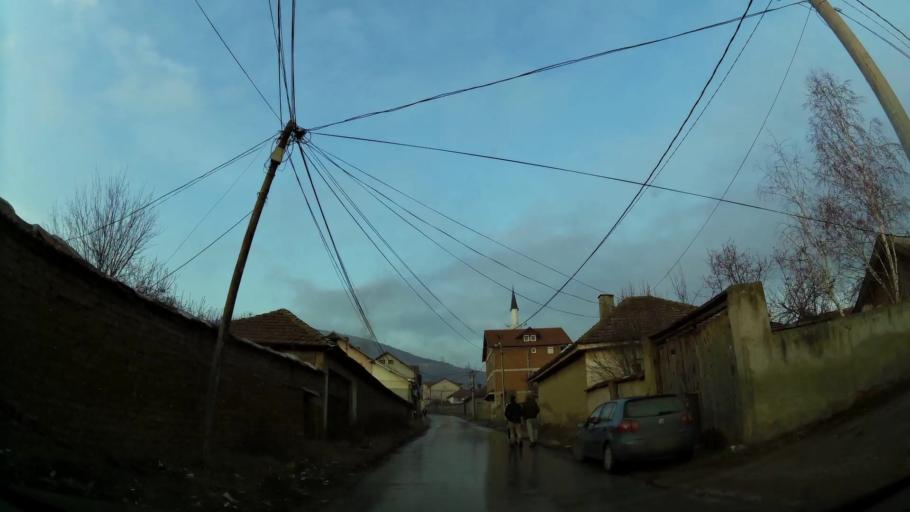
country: MK
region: Aracinovo
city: Arachinovo
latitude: 42.0296
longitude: 21.5652
